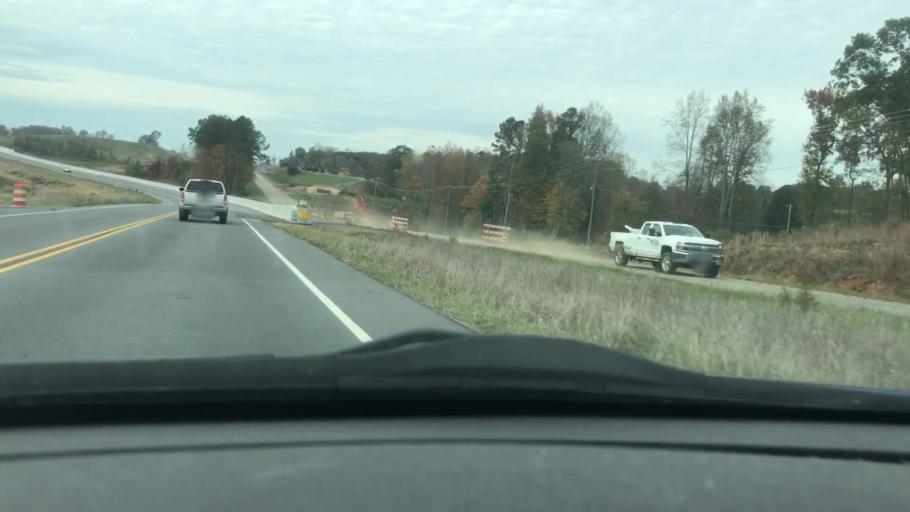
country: US
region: North Carolina
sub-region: Randolph County
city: Asheboro
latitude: 35.6958
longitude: -79.8638
